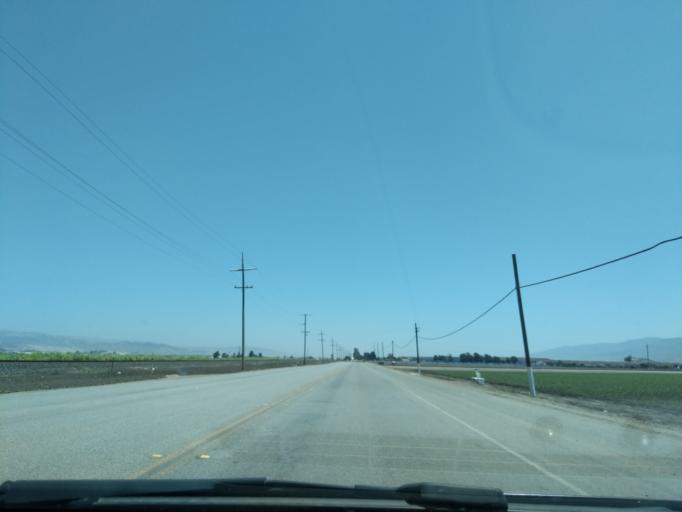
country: US
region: California
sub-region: Monterey County
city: Salinas
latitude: 36.6354
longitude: -121.5991
